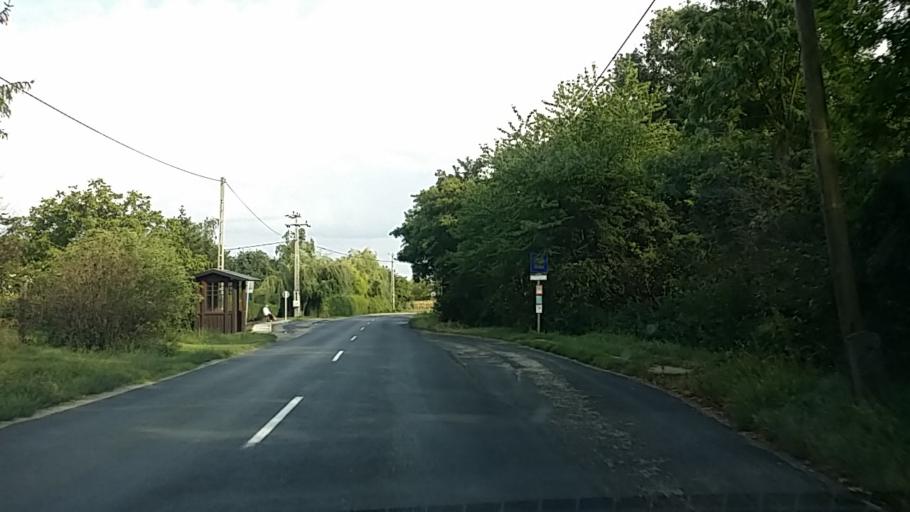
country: HU
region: Gyor-Moson-Sopron
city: Sopron
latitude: 47.6730
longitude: 16.6318
